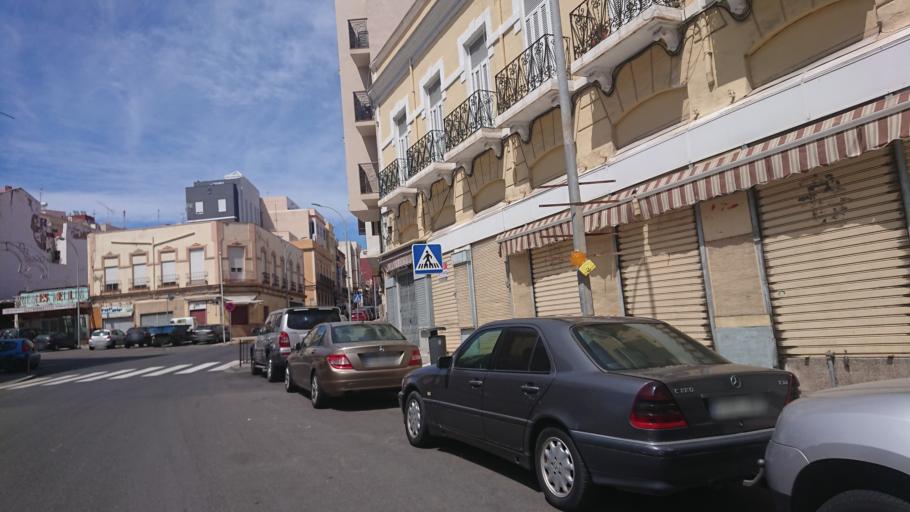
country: ES
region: Melilla
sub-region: Melilla
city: Melilla
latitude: 35.2950
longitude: -2.9421
